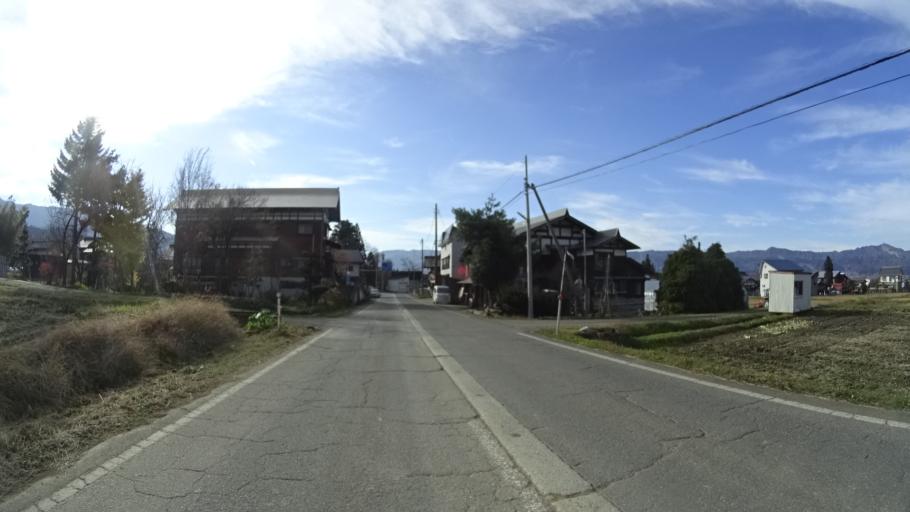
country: JP
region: Niigata
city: Shiozawa
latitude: 37.0148
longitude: 138.8814
